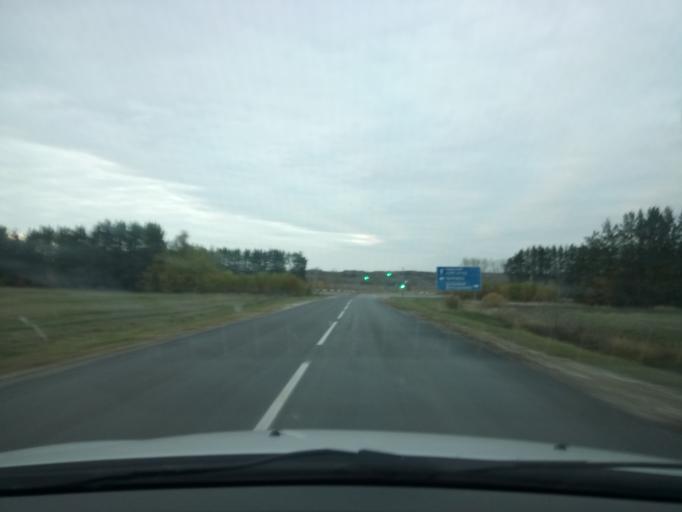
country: RU
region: Nizjnij Novgorod
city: Bol'shoye Murashkino
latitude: 55.7906
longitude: 44.7398
